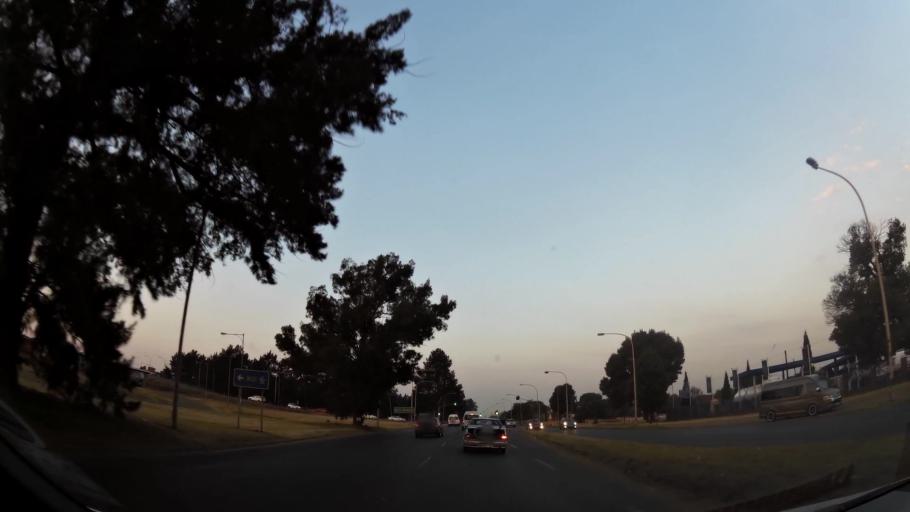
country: ZA
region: Gauteng
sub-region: Ekurhuleni Metropolitan Municipality
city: Springs
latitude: -26.2670
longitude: 28.4165
